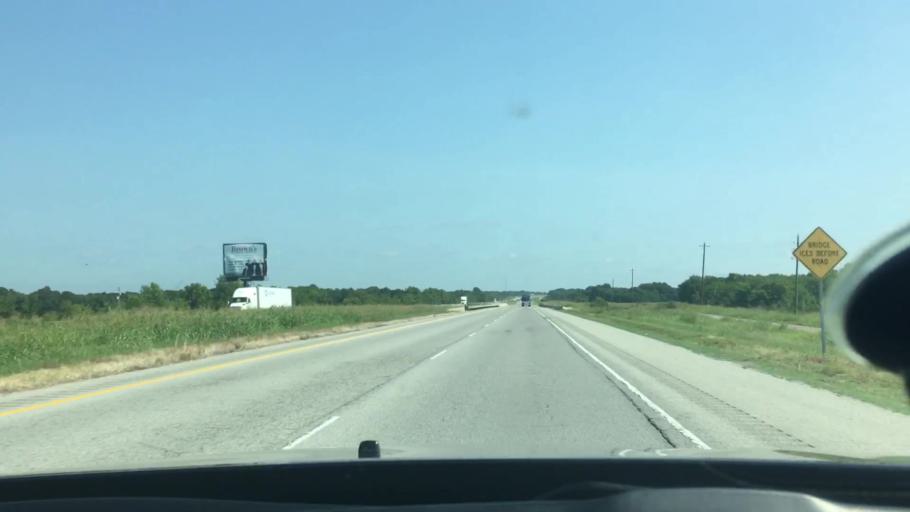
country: US
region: Oklahoma
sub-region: Atoka County
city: Atoka
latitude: 34.2460
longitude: -96.2171
